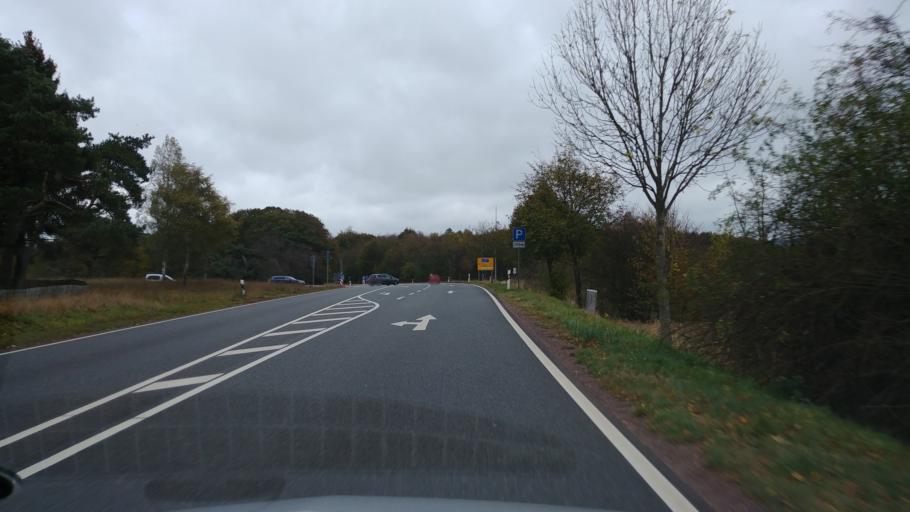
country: DE
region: Rheinland-Pfalz
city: Gielert
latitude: 49.7634
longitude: 7.0043
